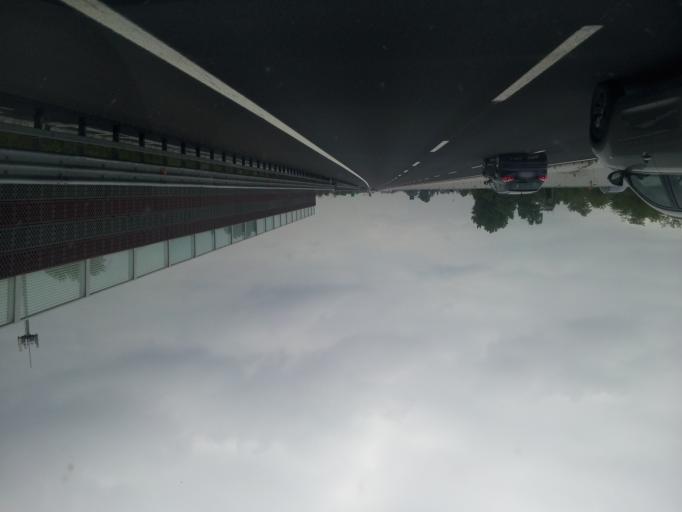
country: IT
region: Veneto
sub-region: Provincia di Venezia
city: Meolo
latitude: 45.6170
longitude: 12.4161
